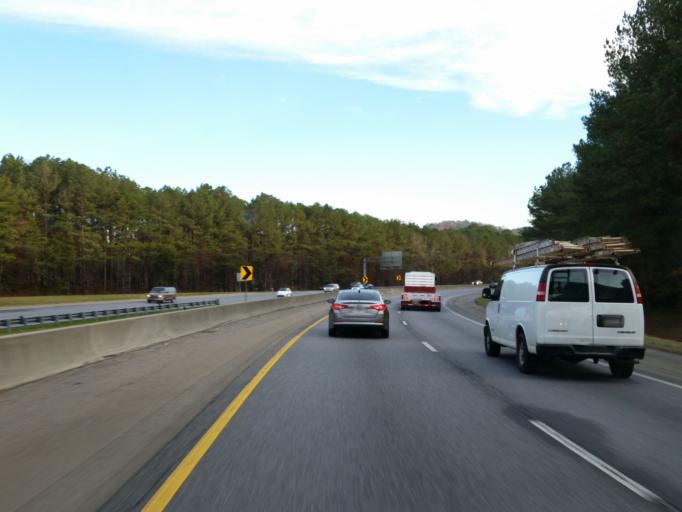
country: US
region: Georgia
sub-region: Cherokee County
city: Canton
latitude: 34.2197
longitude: -84.4892
